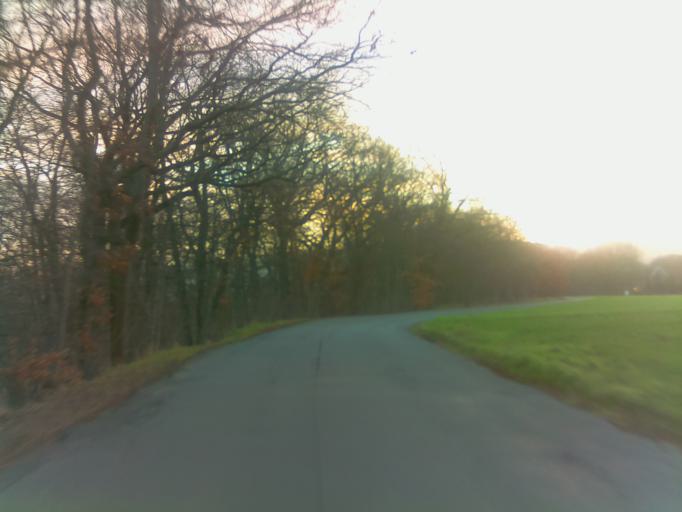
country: DE
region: Thuringia
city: Rudolstadt
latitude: 50.7192
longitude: 11.3817
